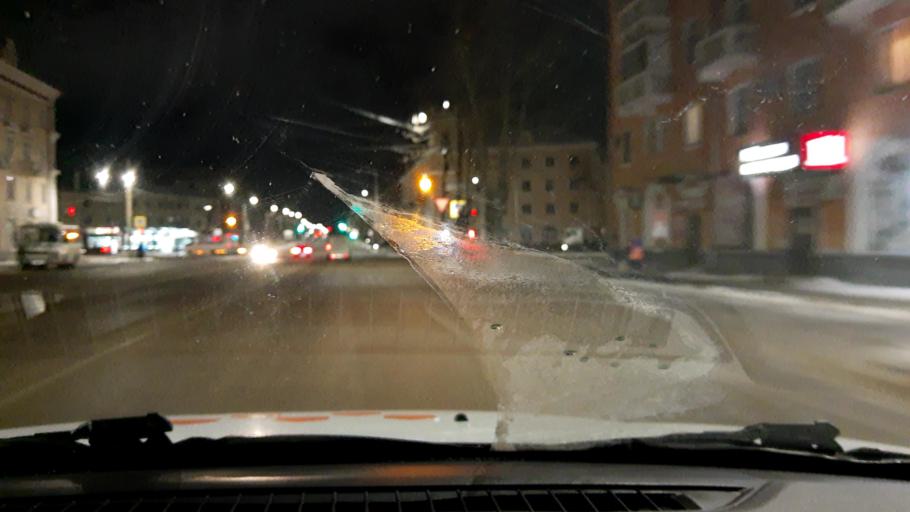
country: RU
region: Nizjnij Novgorod
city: Dzerzhinsk
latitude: 56.2389
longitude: 43.4850
